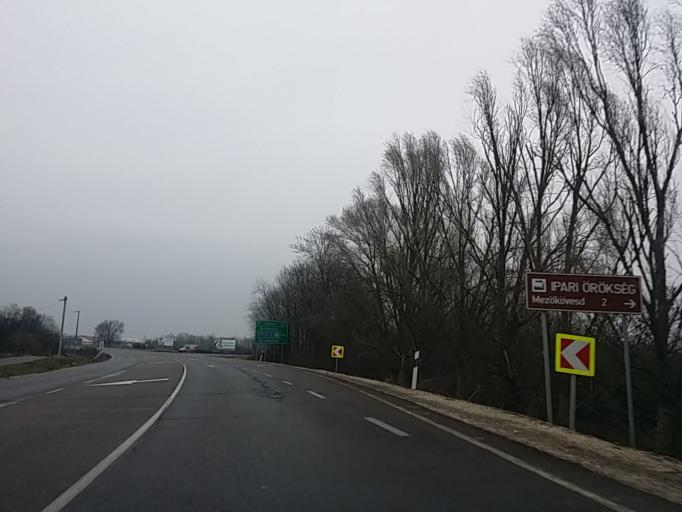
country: HU
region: Borsod-Abauj-Zemplen
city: Mezokovesd
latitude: 47.7974
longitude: 20.5380
